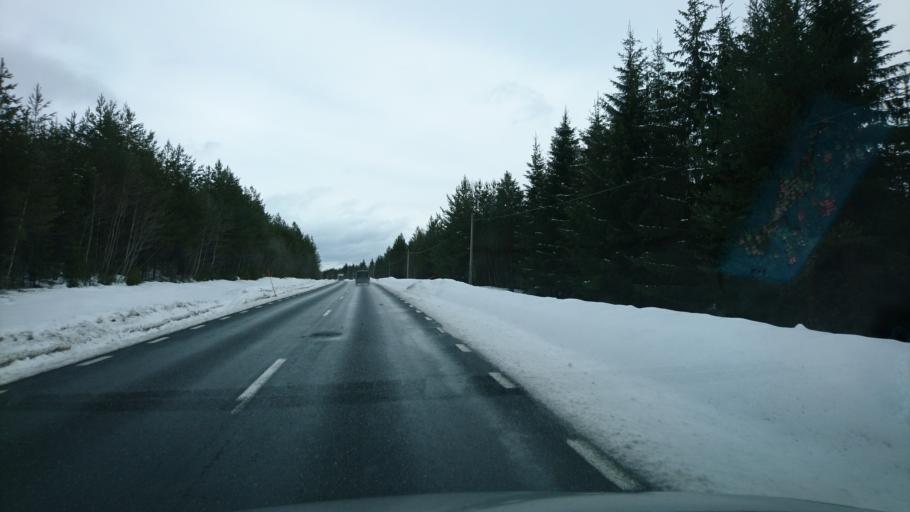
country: SE
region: Vaesternorrland
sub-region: Solleftea Kommun
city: Solleftea
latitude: 63.0532
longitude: 17.0444
